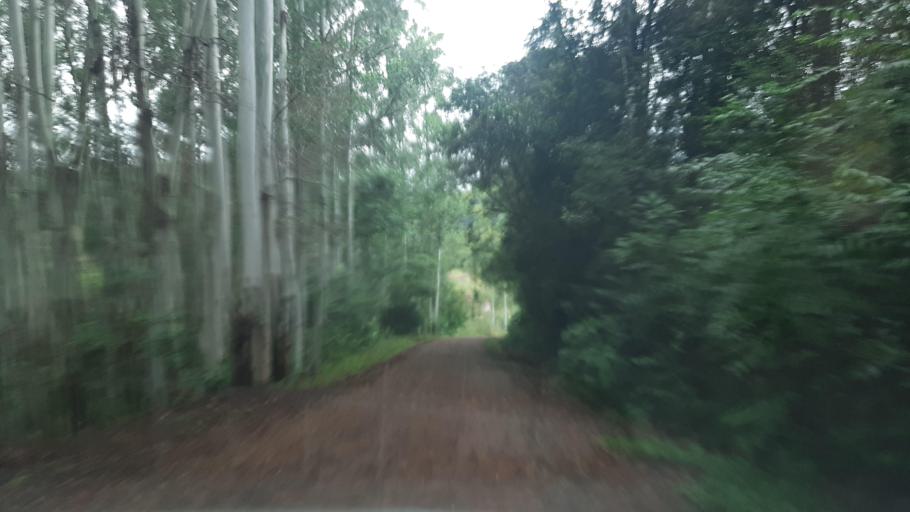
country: BR
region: Parana
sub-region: Ampere
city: Ampere
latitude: -26.0404
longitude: -53.5137
